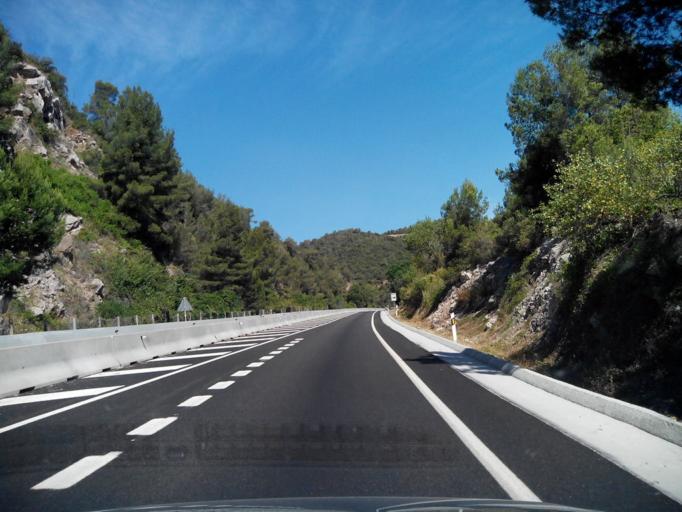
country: ES
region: Catalonia
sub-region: Provincia de Barcelona
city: Viladecavalls
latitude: 41.5818
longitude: 1.9541
